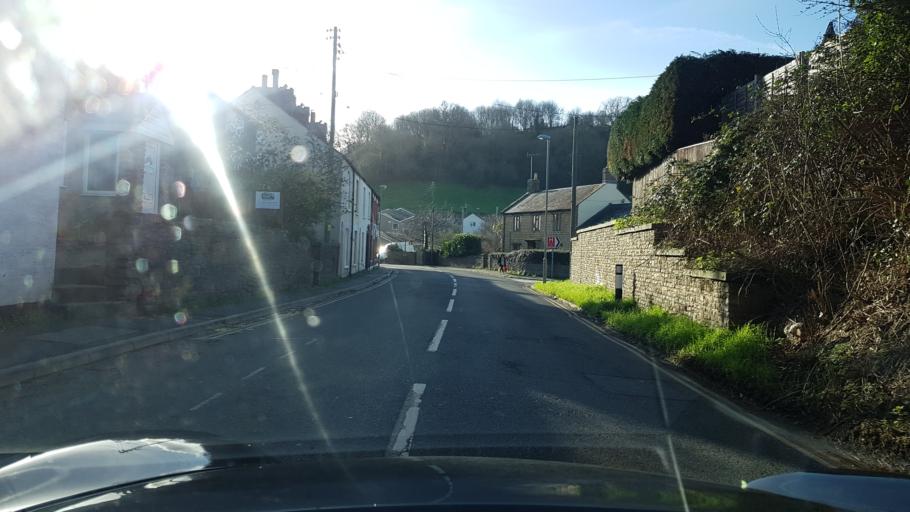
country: GB
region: England
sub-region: Dorset
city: Bridport
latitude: 50.7404
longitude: -2.7656
